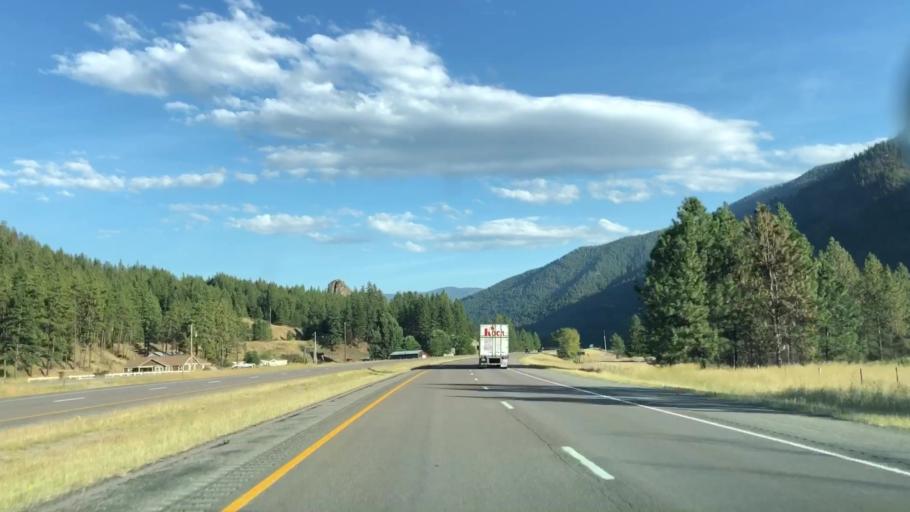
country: US
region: Montana
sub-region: Missoula County
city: Frenchtown
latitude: 47.0150
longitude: -114.5059
